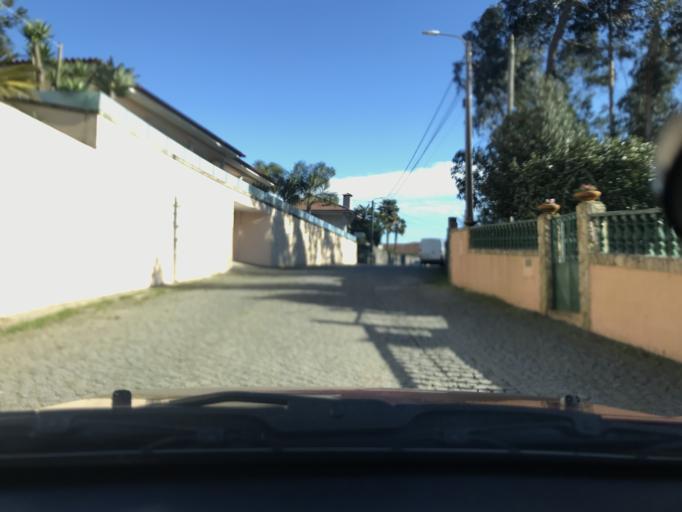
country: PT
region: Braga
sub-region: Vila Nova de Famalicao
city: Vila Nova de Famalicao
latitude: 41.4207
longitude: -8.5088
